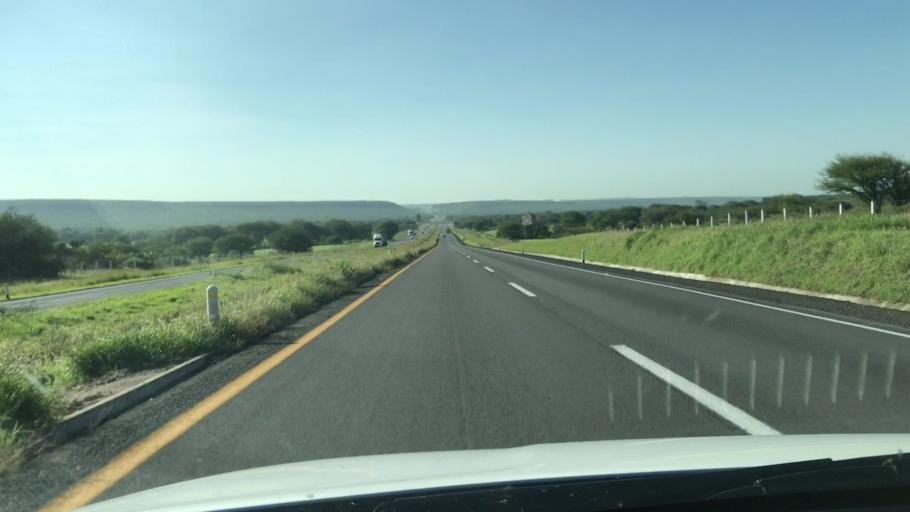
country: MX
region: Jalisco
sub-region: Union de San Antonio
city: San Jose del Caliche (El Caliche)
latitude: 21.1662
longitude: -101.8629
